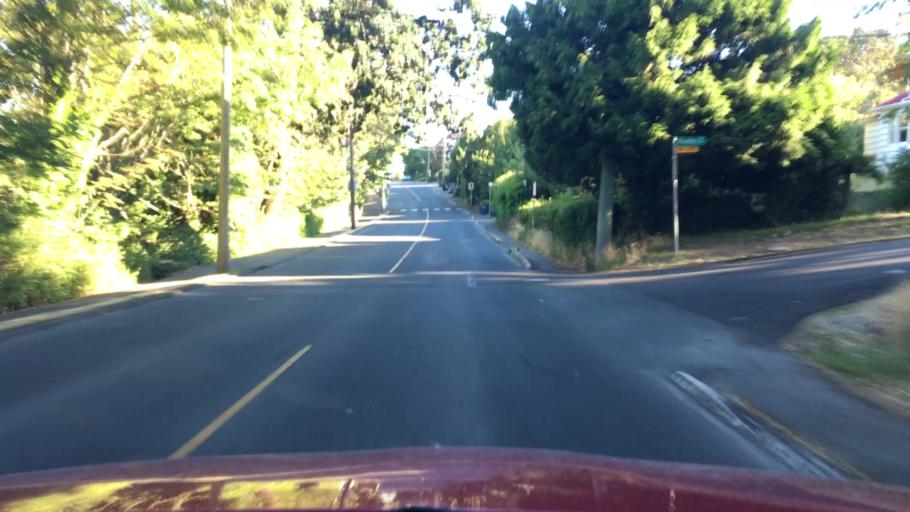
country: CA
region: British Columbia
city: Oak Bay
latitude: 48.4519
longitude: -123.3262
